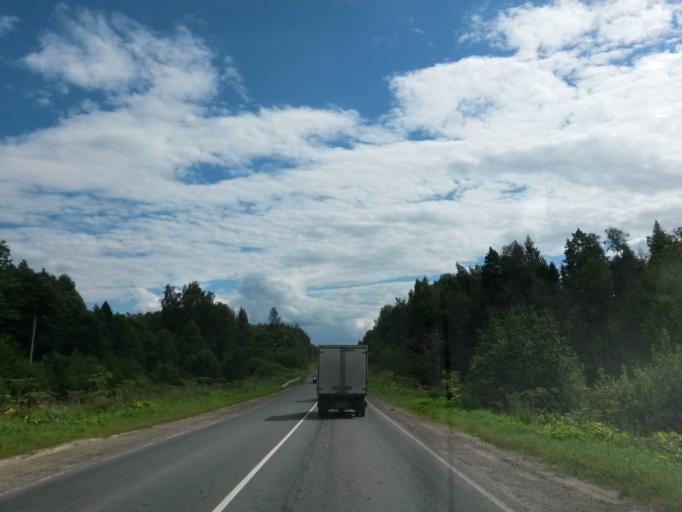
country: RU
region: Ivanovo
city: Novo-Talitsy
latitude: 57.0599
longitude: 40.7214
